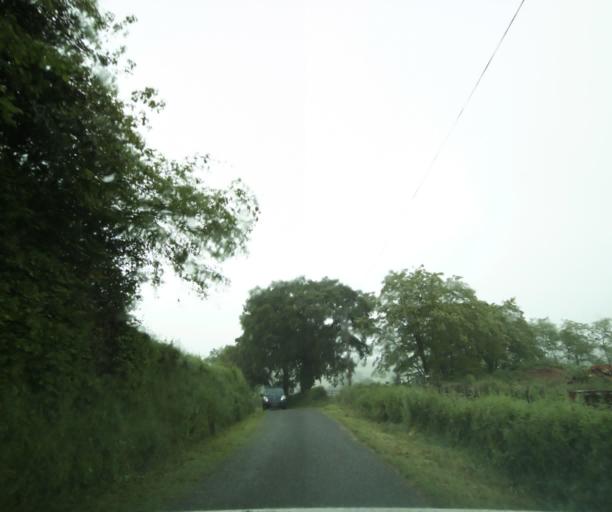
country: FR
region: Bourgogne
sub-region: Departement de Saone-et-Loire
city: Charolles
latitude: 46.4041
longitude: 4.3930
